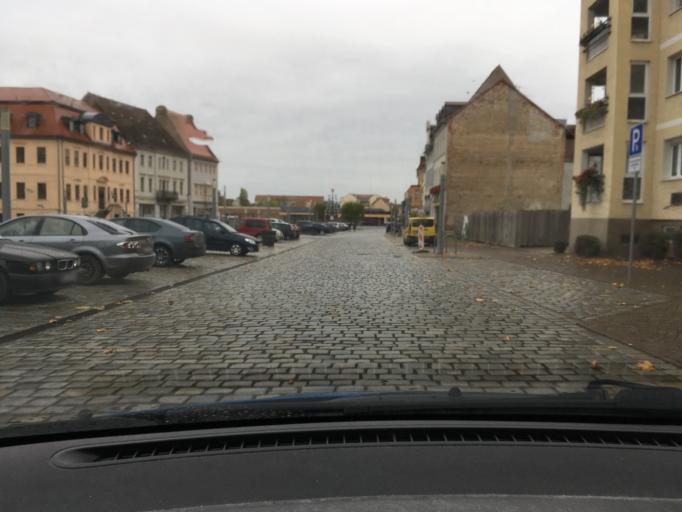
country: DE
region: Saxony-Anhalt
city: Zerbst
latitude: 51.9686
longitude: 12.0842
